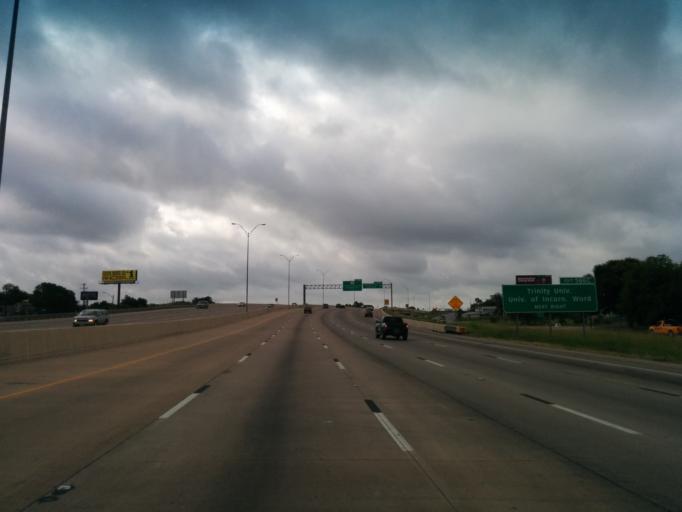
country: US
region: Texas
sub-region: Bexar County
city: Olmos Park
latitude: 29.4766
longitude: -98.5197
